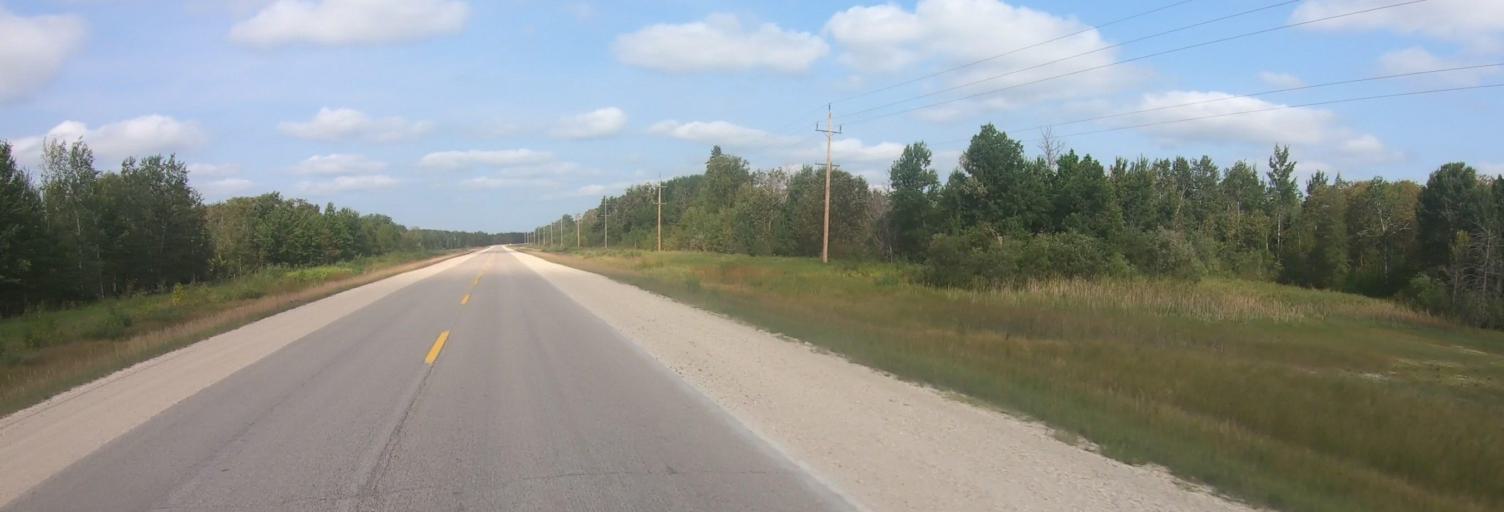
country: CA
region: Manitoba
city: La Broquerie
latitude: 49.2328
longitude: -96.3343
